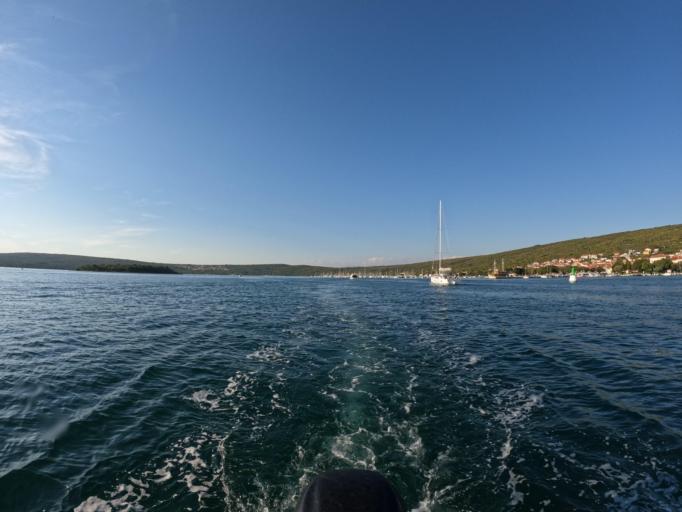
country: HR
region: Primorsko-Goranska
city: Punat
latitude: 45.0199
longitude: 14.6244
